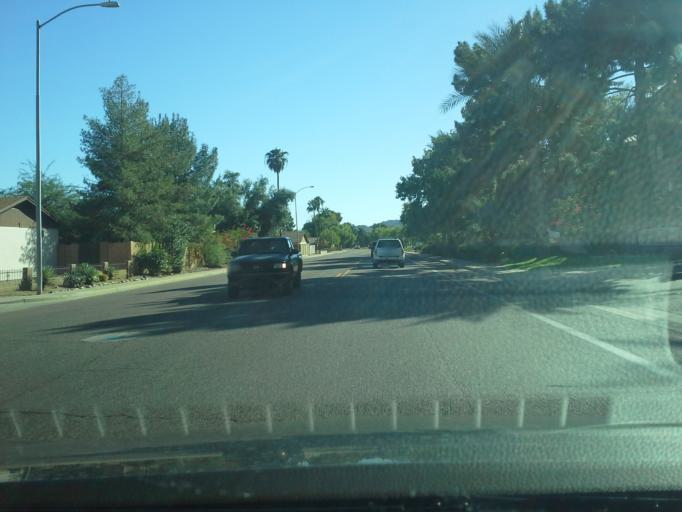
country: US
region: Arizona
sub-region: Maricopa County
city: Paradise Valley
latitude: 33.6083
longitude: -111.9866
